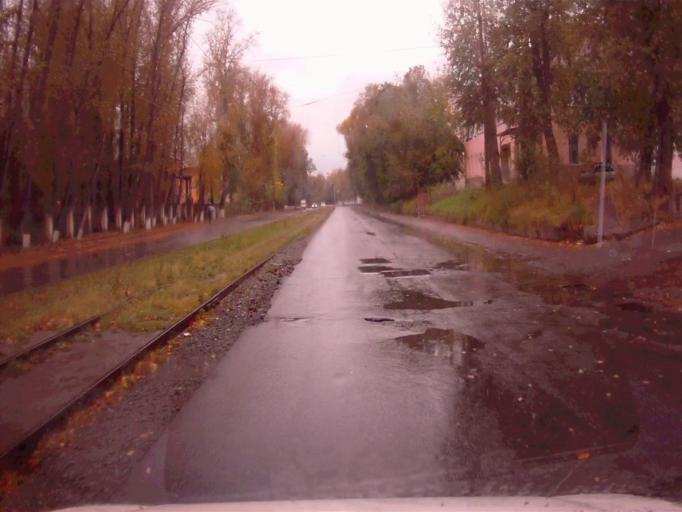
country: RU
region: Chelyabinsk
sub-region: Gorod Chelyabinsk
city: Chelyabinsk
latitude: 55.1888
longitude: 61.4131
